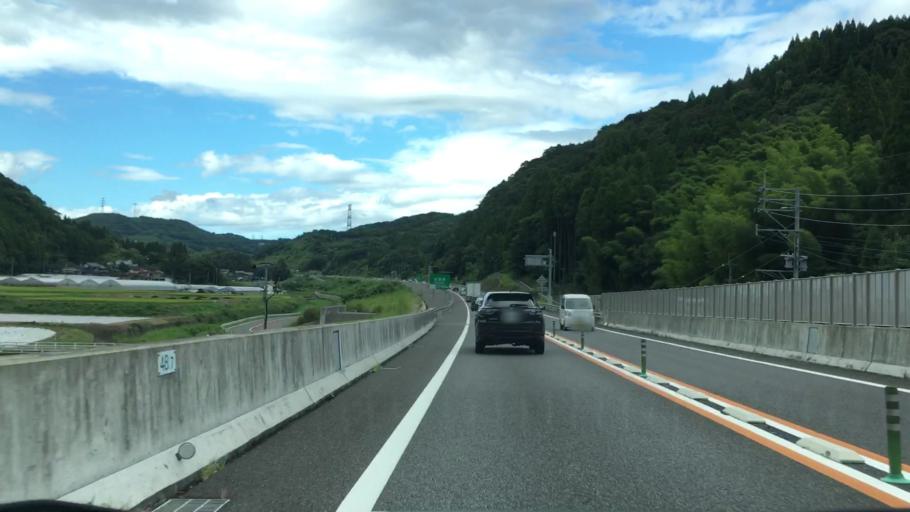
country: JP
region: Saga Prefecture
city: Karatsu
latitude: 33.3767
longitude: 129.9323
